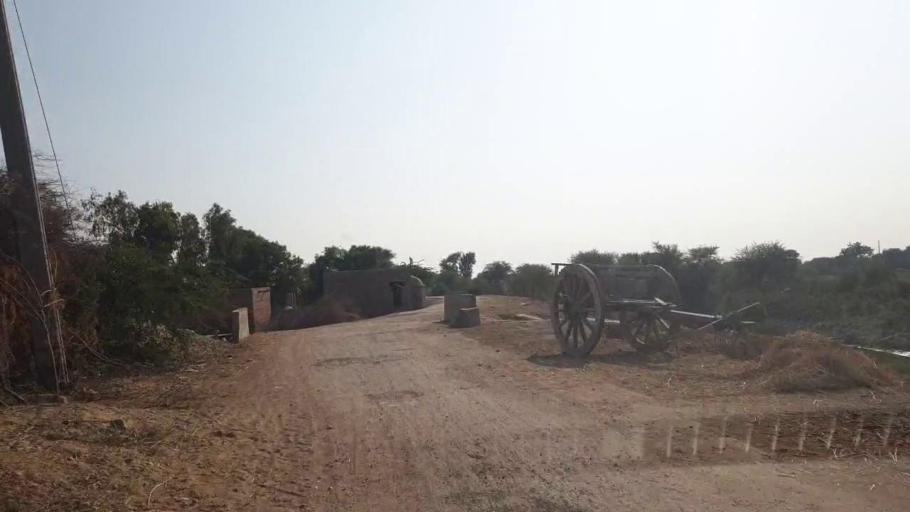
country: PK
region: Sindh
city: Kario
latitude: 24.9183
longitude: 68.6518
